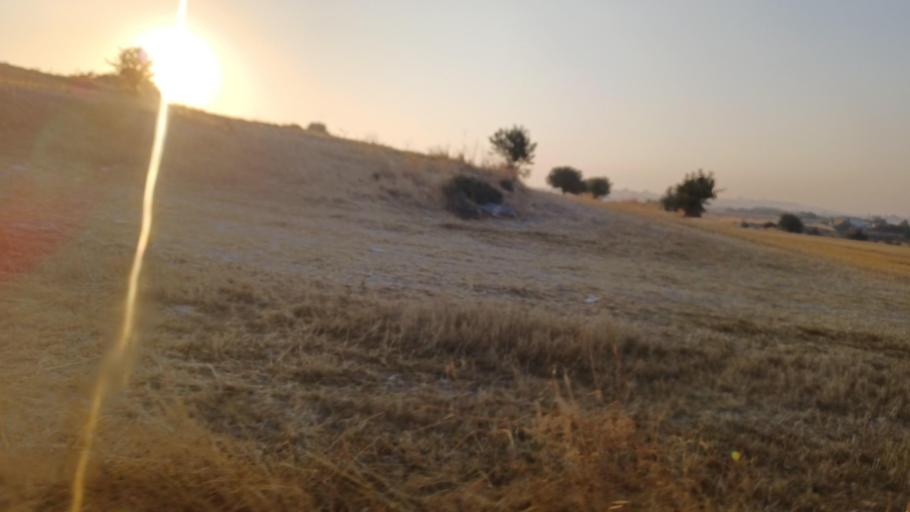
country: CY
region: Larnaka
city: Tersefanou
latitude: 34.9006
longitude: 33.5149
